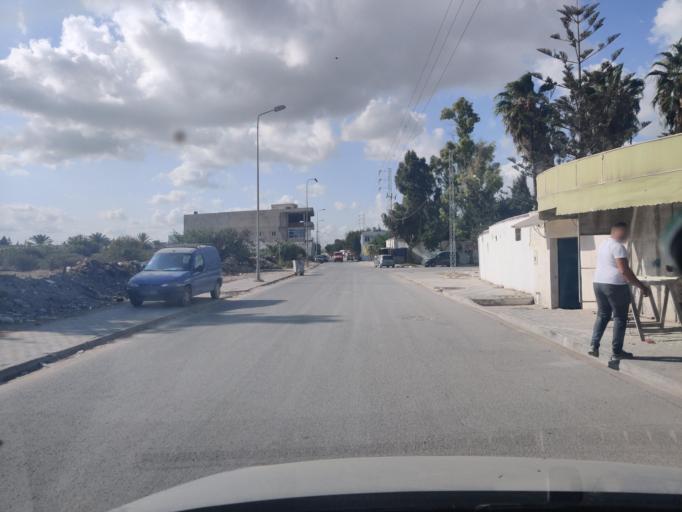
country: TN
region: Tunis
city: Al Marsa
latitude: 36.8786
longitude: 10.2725
